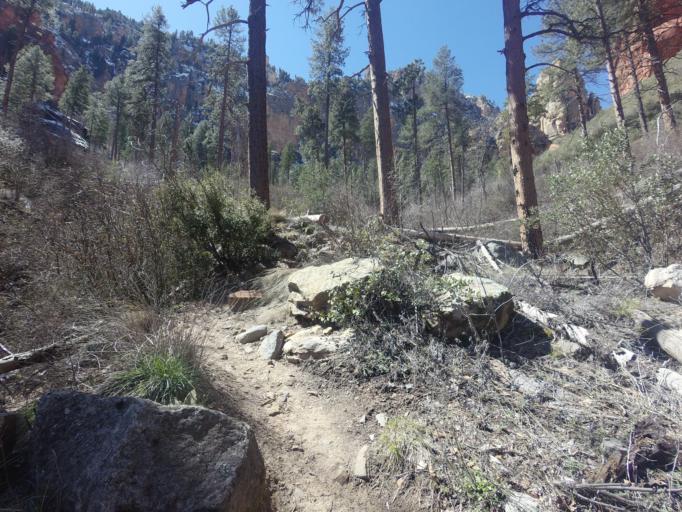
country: US
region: Arizona
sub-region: Coconino County
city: Sedona
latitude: 34.9340
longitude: -111.7546
